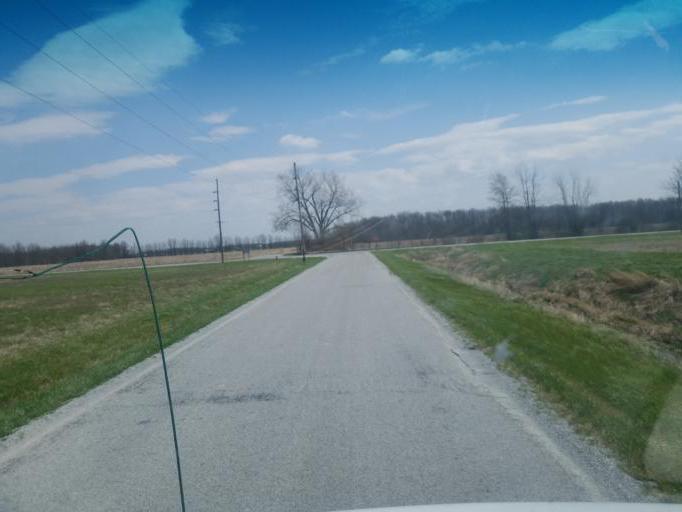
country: US
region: Ohio
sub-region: Hardin County
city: Forest
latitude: 40.7595
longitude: -83.4976
